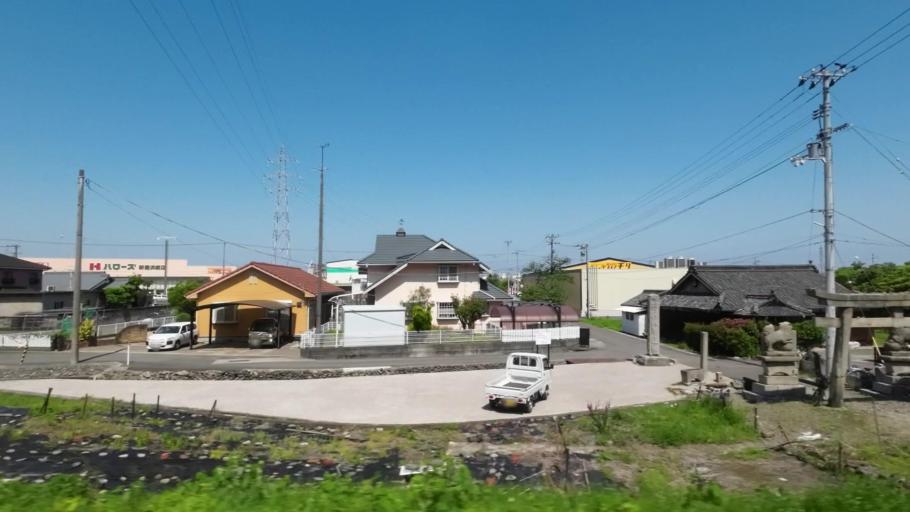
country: JP
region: Ehime
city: Niihama
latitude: 33.9569
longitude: 133.3045
